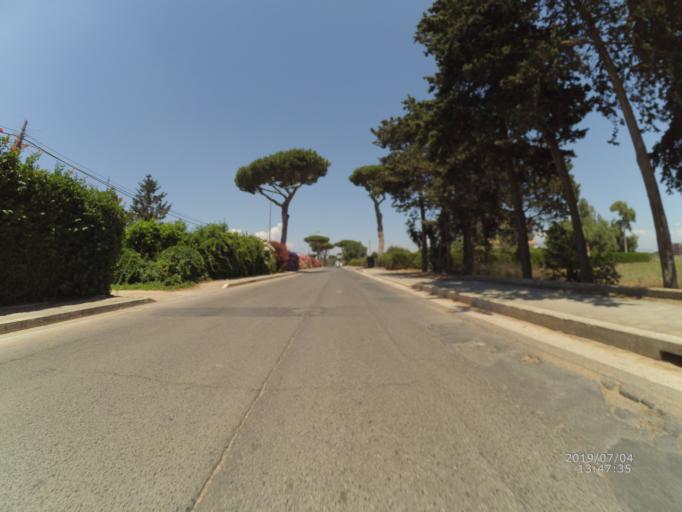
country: IT
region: Latium
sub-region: Provincia di Latina
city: San Felice Circeo
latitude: 41.2787
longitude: 13.1020
